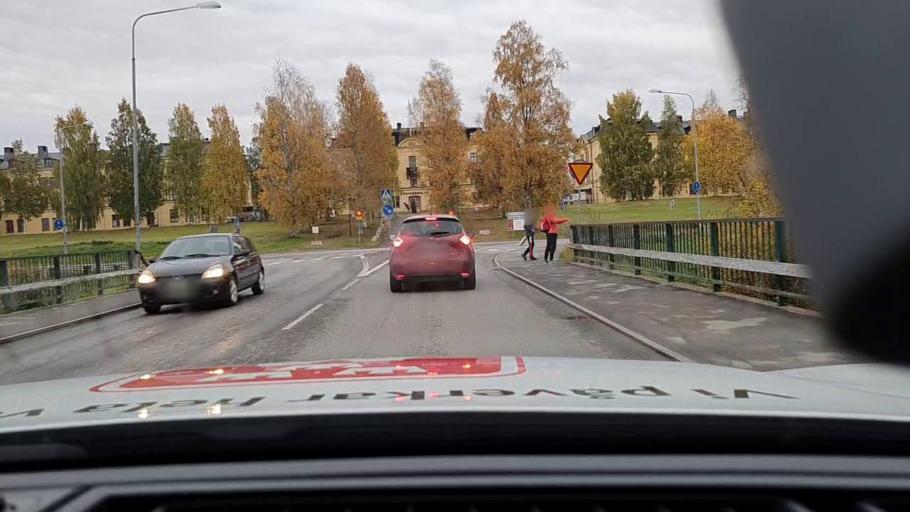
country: SE
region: Norrbotten
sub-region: Bodens Kommun
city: Boden
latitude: 65.8140
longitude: 21.6777
